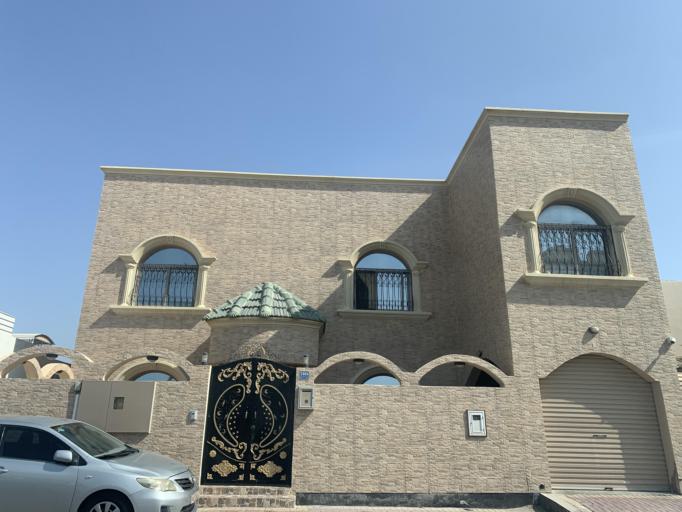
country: BH
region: Central Governorate
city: Madinat Hamad
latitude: 26.1339
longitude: 50.5051
